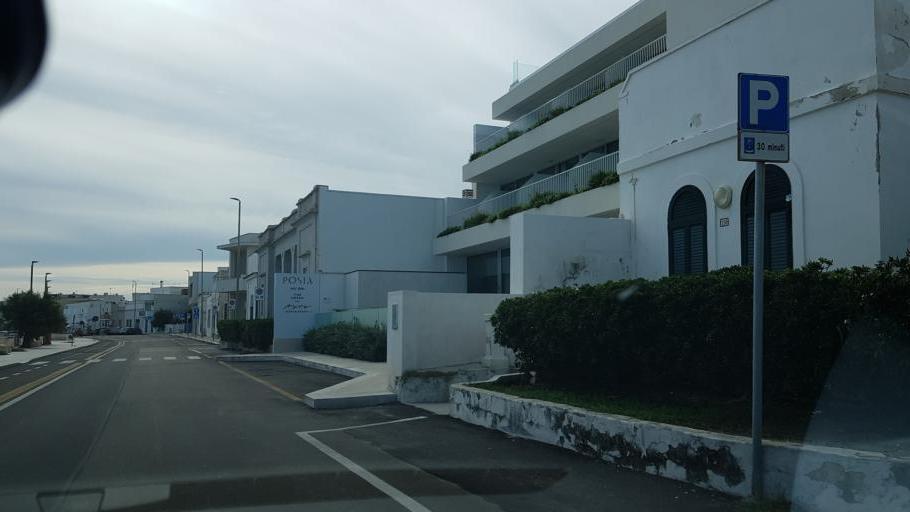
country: IT
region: Apulia
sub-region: Provincia di Lecce
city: Borgagne
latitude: 40.3044
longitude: 18.3999
